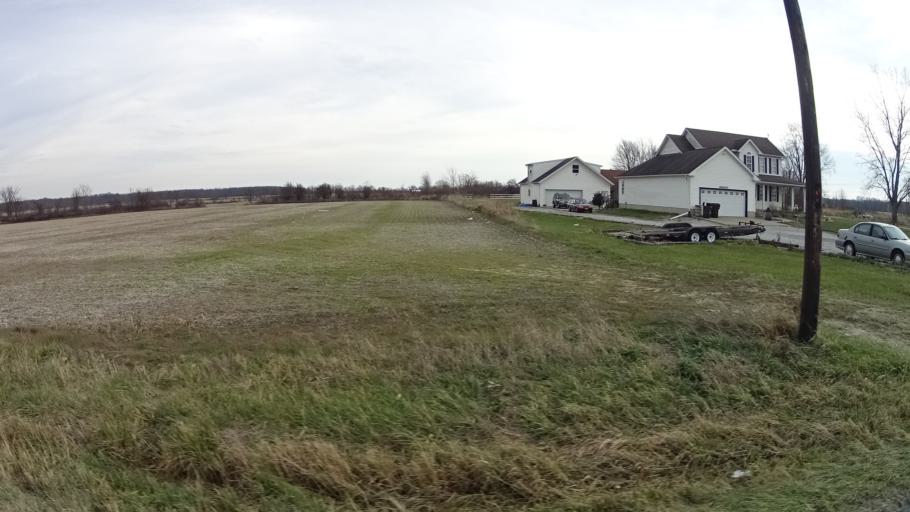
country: US
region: Ohio
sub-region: Lorain County
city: Wellington
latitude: 41.1702
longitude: -82.1692
